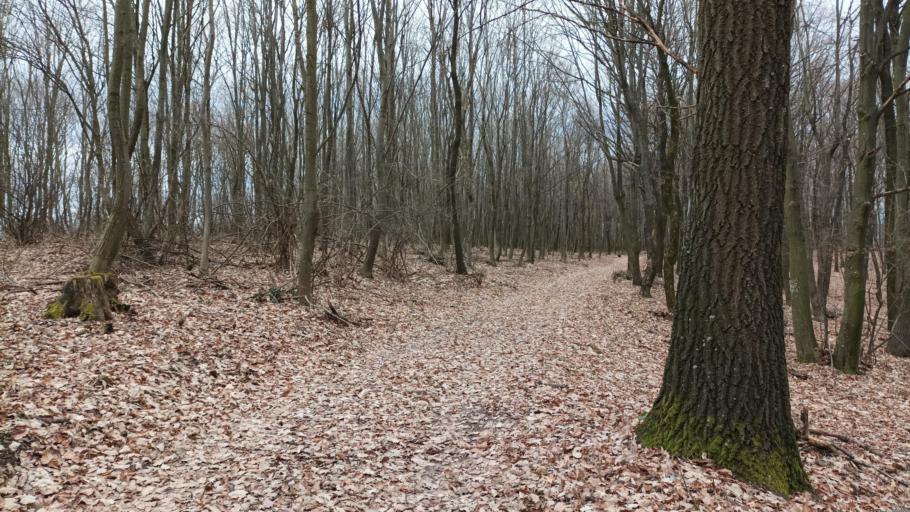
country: HU
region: Tolna
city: Szentgalpuszta
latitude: 46.3304
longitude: 18.6375
